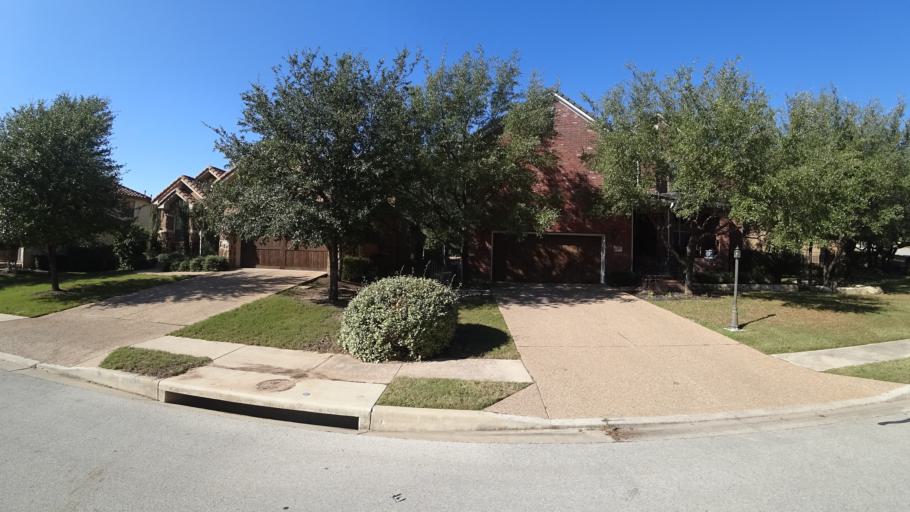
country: US
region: Texas
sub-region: Travis County
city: Hudson Bend
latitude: 30.3590
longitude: -97.8847
